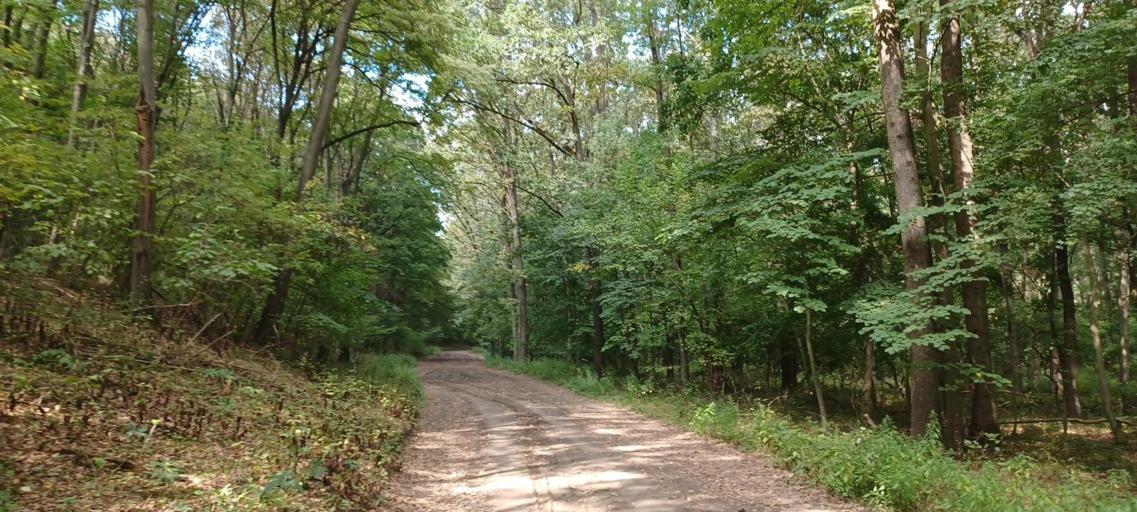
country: HU
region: Tolna
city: Szentgalpuszta
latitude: 46.3337
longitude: 18.6184
